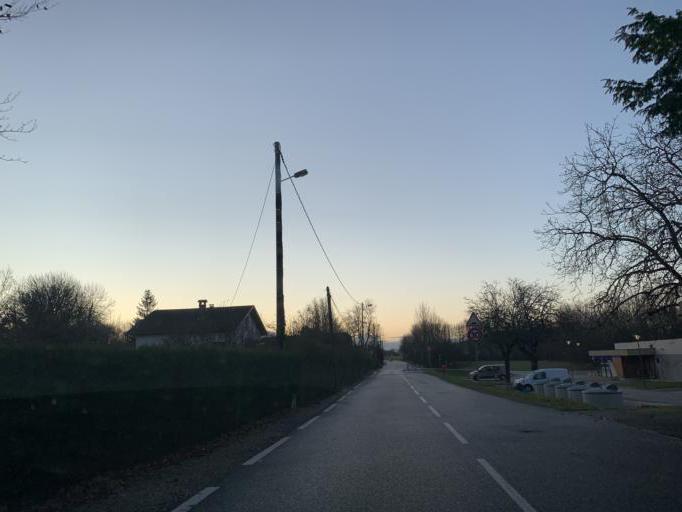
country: FR
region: Rhone-Alpes
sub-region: Departement de l'Ain
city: Virieu-le-Grand
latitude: 45.8036
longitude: 5.6287
